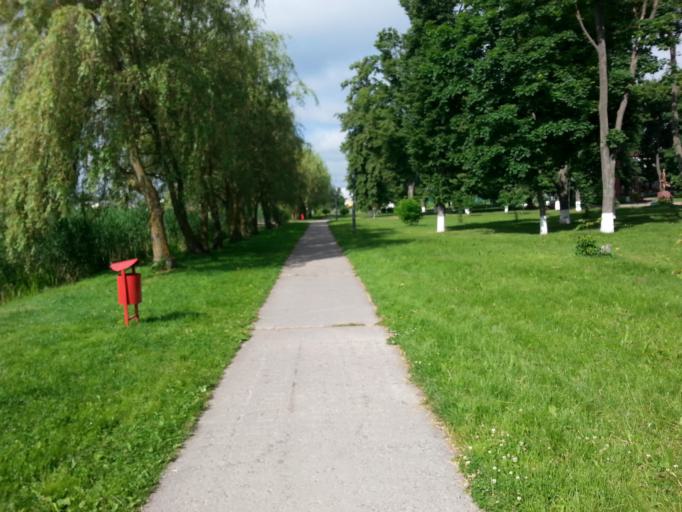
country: BY
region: Vitebsk
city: Hlybokaye
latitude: 55.1386
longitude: 27.6913
